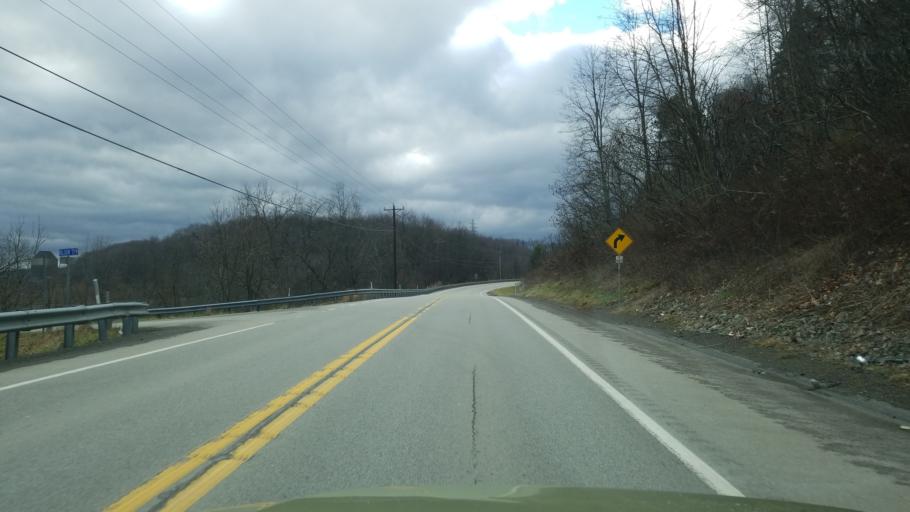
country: US
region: Pennsylvania
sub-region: Indiana County
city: Clymer
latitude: 40.8118
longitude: -79.0519
